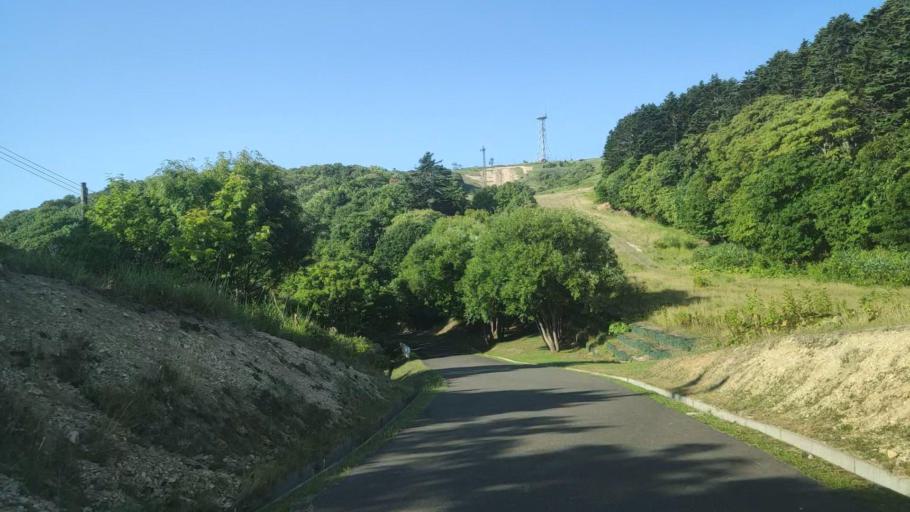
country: JP
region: Hokkaido
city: Wakkanai
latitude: 45.4159
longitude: 141.6677
